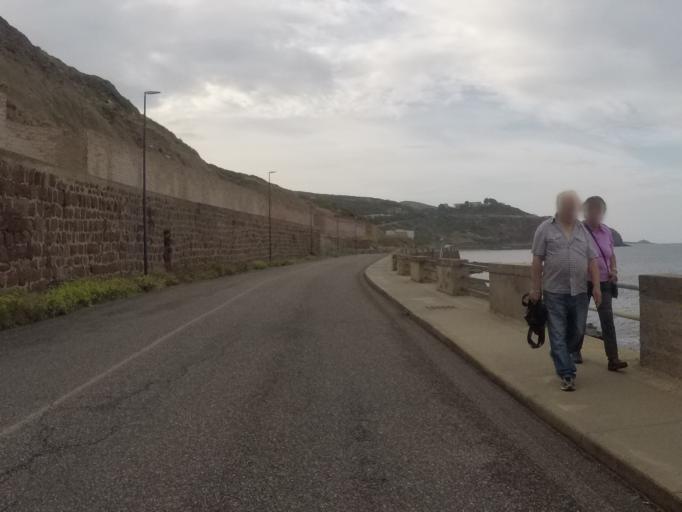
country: IT
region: Sardinia
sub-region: Provincia di Oristano
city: Bosa
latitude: 40.2788
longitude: 8.4839
